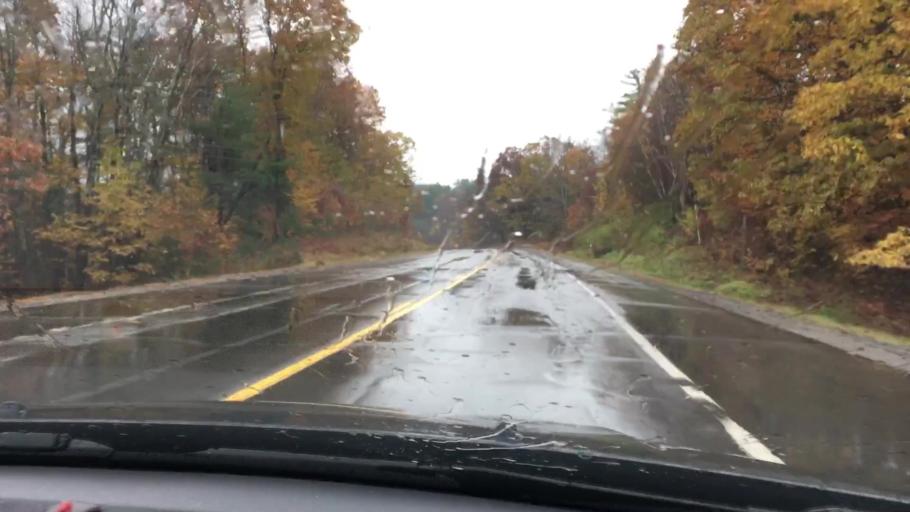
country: US
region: New Hampshire
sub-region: Grafton County
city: Ashland
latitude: 43.7068
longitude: -71.6295
